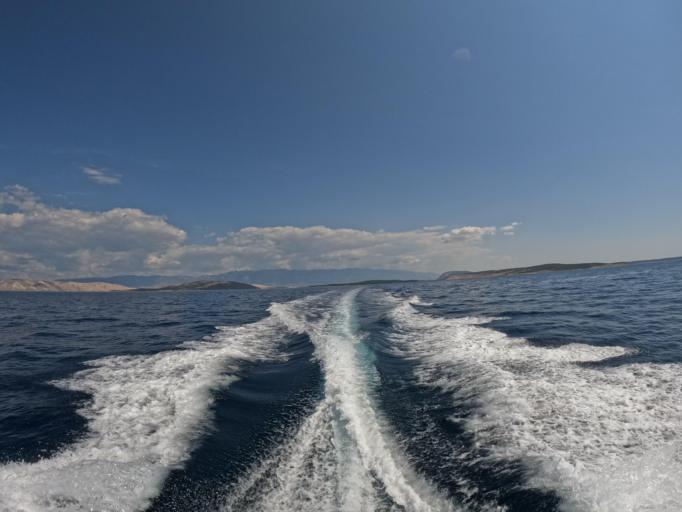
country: HR
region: Primorsko-Goranska
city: Lopar
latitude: 44.8710
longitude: 14.6727
